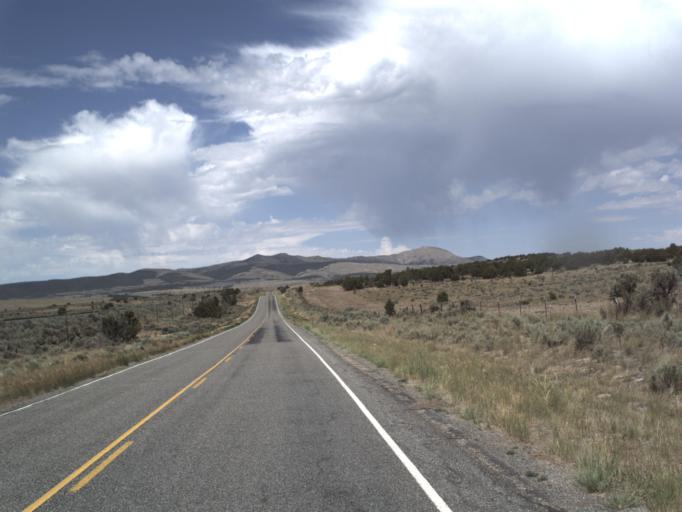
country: US
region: Utah
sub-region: Utah County
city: Genola
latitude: 39.9439
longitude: -112.1991
